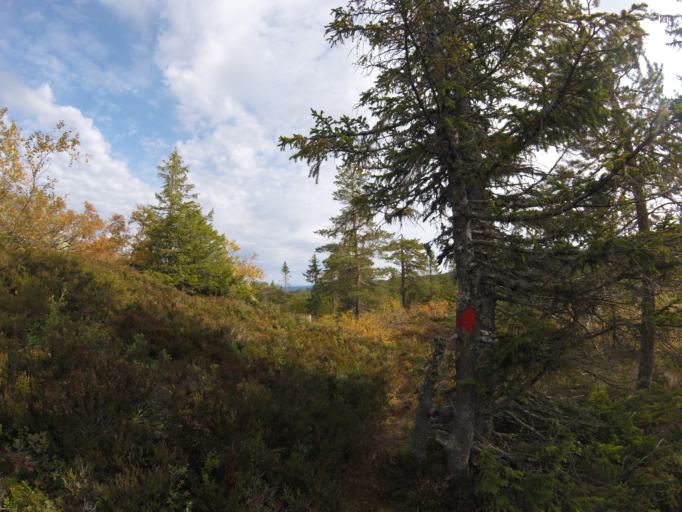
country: NO
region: Buskerud
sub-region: Rollag
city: Rollag
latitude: 59.8112
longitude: 9.3316
